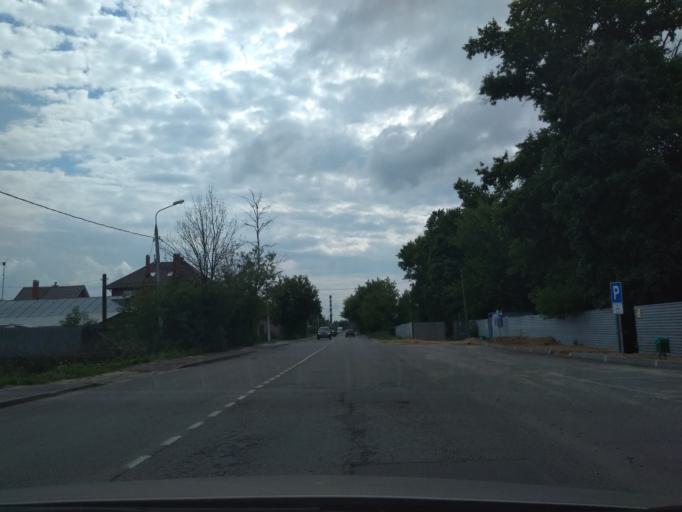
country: RU
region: Moskovskaya
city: Orekhovo-Zuyevo
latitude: 55.8036
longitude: 38.9540
